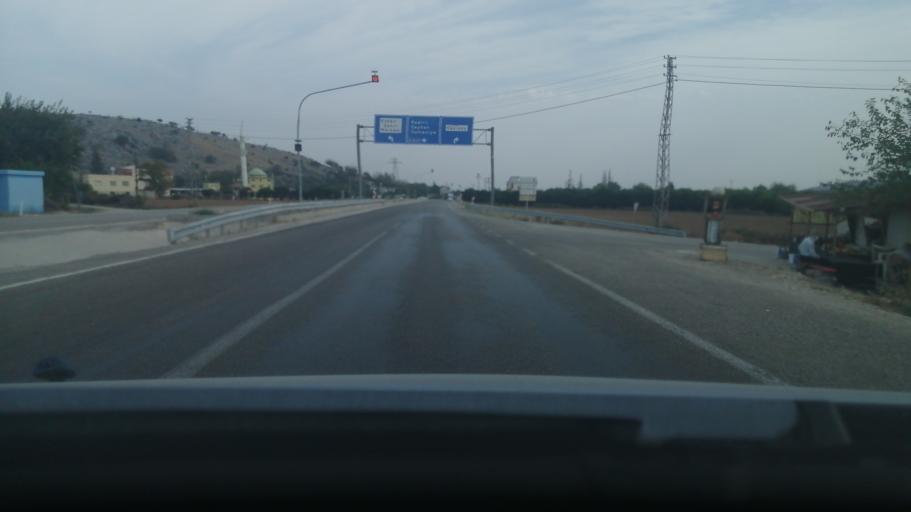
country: TR
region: Adana
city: Kozan
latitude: 37.3811
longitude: 35.8227
